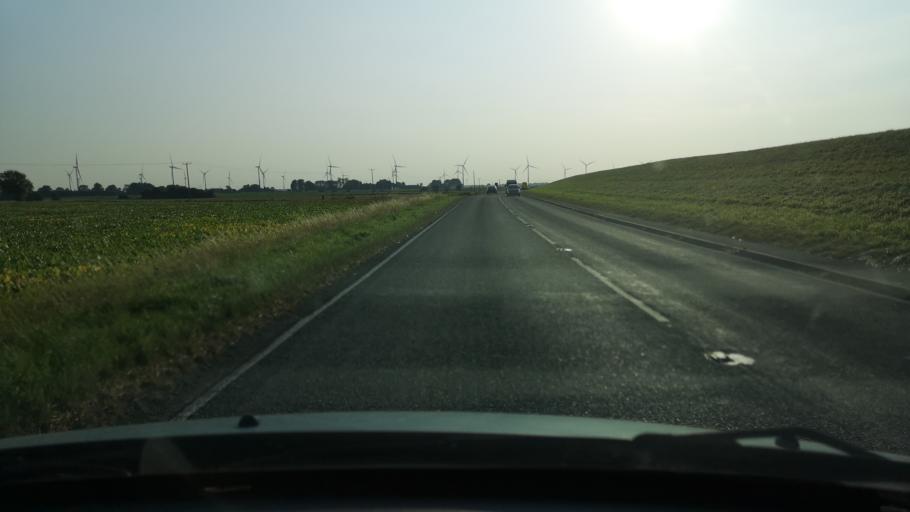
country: GB
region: England
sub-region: East Riding of Yorkshire
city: Skelton
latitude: 53.6848
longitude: -0.8461
